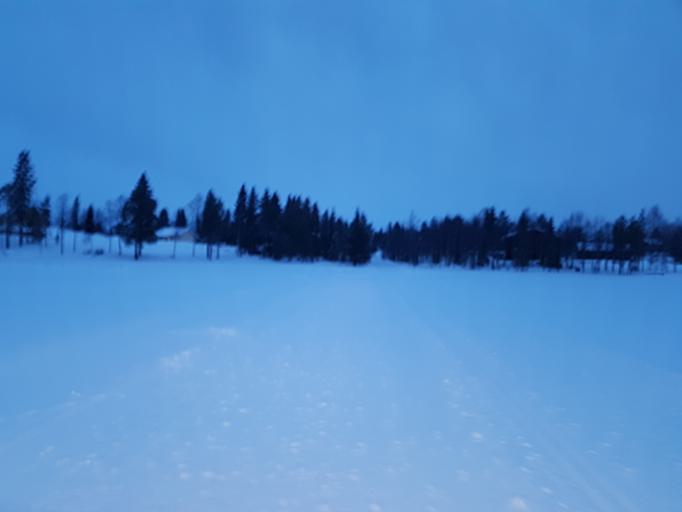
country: FI
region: Lapland
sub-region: Tunturi-Lappi
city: Kolari
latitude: 67.6117
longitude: 24.1484
